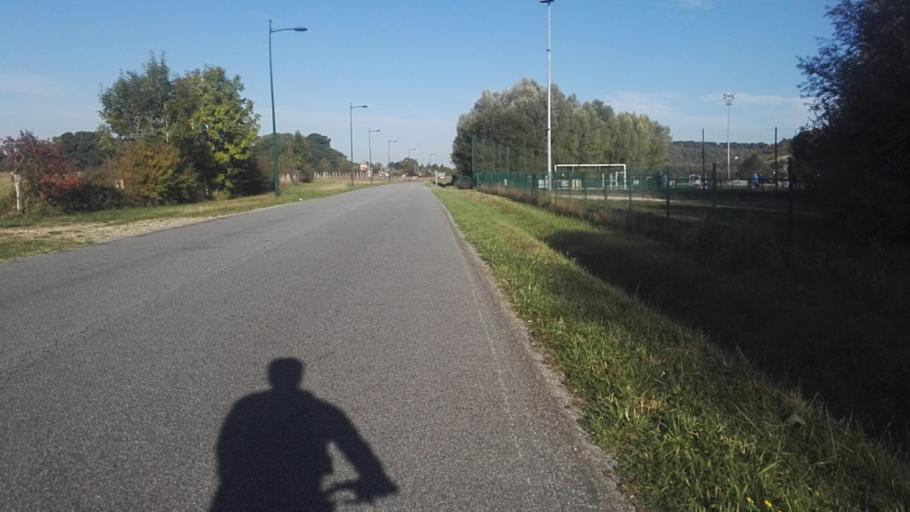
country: FR
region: Haute-Normandie
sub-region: Departement de l'Eure
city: Menilles
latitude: 49.0261
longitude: 1.3707
